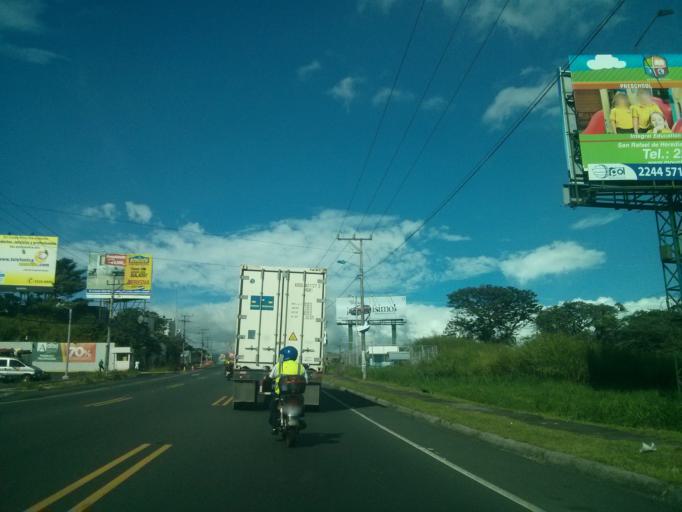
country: CR
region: Heredia
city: San Francisco
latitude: 9.9715
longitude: -84.1139
